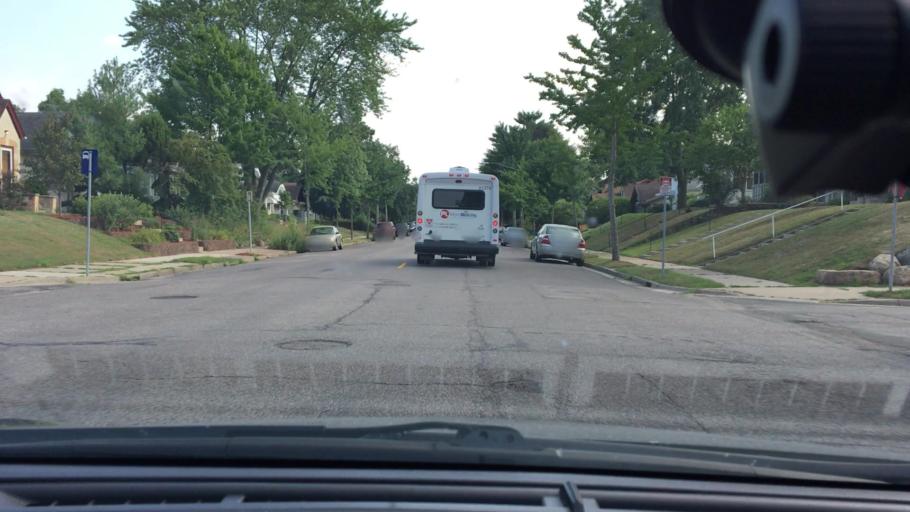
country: US
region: Minnesota
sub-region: Hennepin County
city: Richfield
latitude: 44.9179
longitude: -93.2524
